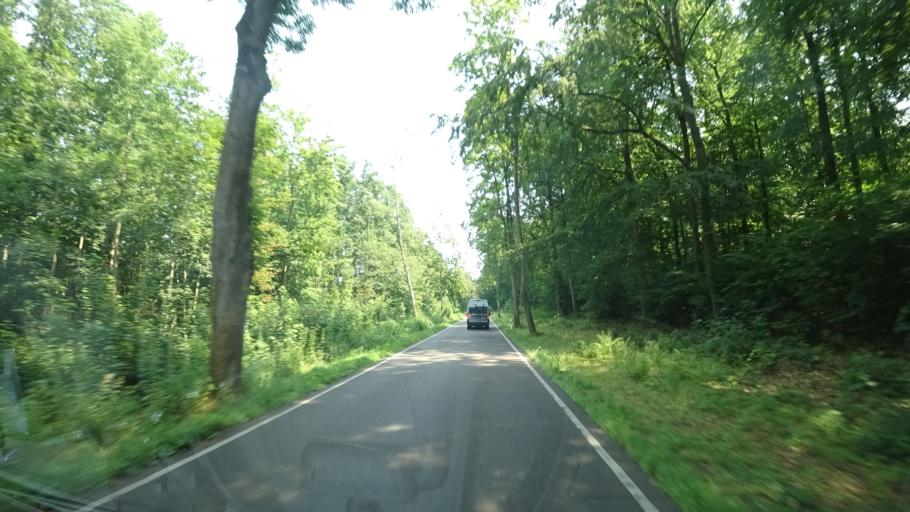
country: PL
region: West Pomeranian Voivodeship
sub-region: Swinoujscie
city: Swinoujscie
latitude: 53.8911
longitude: 14.1885
